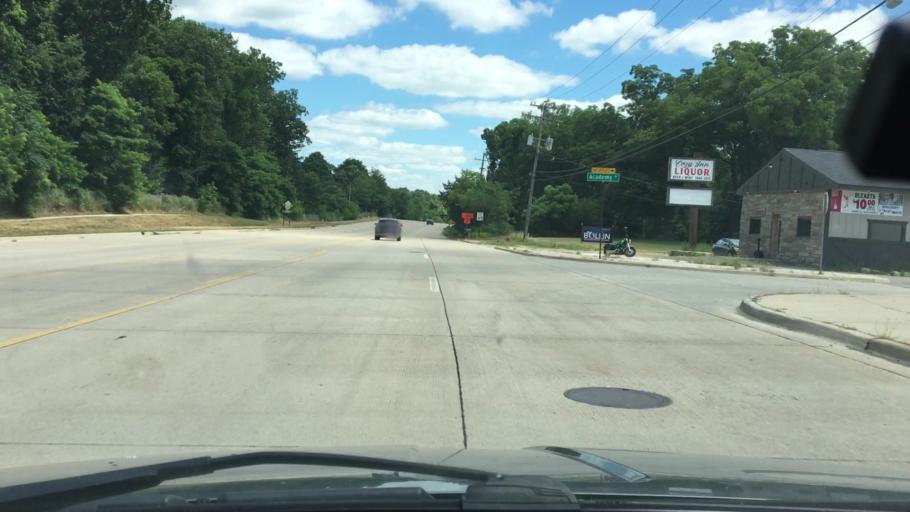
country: US
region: Michigan
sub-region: Livingston County
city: Brighton
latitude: 42.5161
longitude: -83.7364
